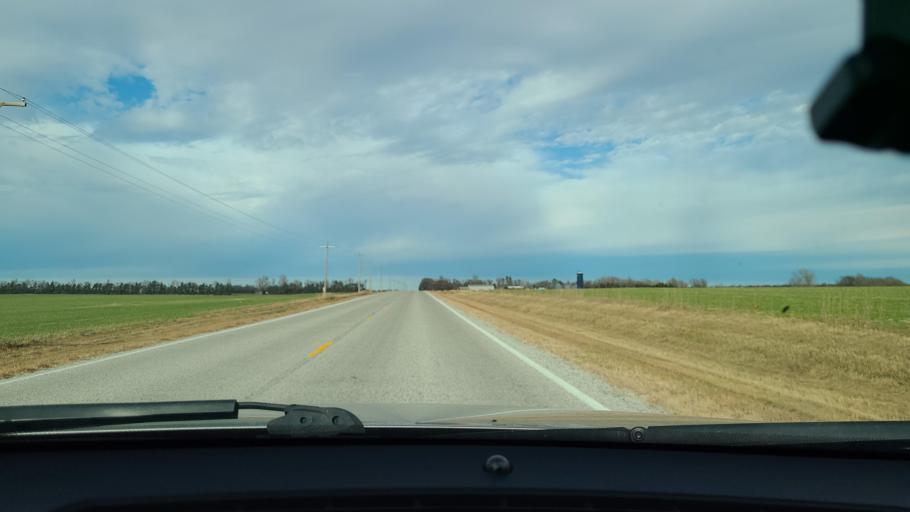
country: US
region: Kansas
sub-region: McPherson County
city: Inman
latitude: 38.3081
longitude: -97.9248
